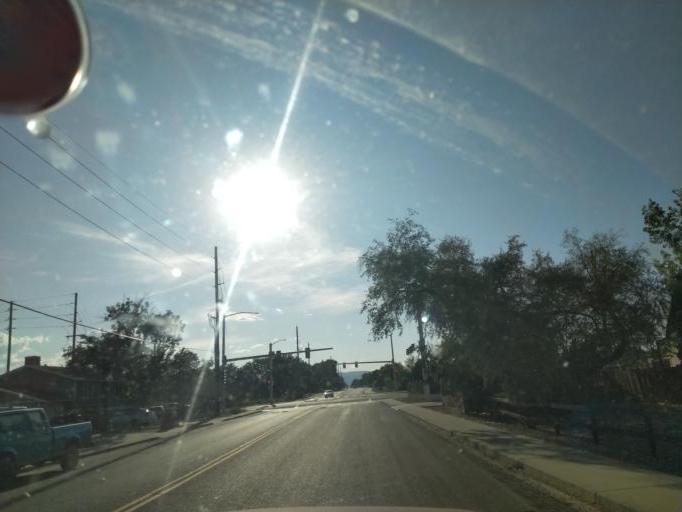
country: US
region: Colorado
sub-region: Mesa County
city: Clifton
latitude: 39.0701
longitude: -108.4584
